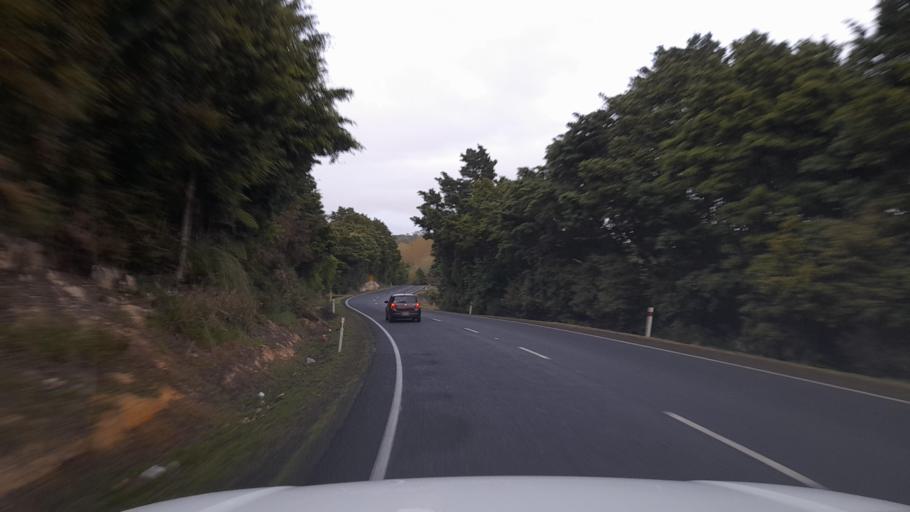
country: NZ
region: Northland
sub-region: Whangarei
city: Maungatapere
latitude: -35.7086
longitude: 174.0068
